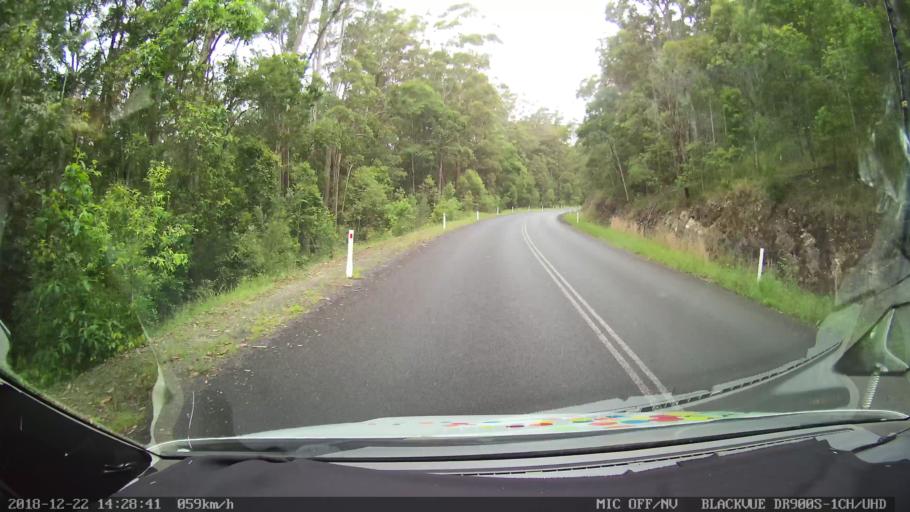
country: AU
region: New South Wales
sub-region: Bellingen
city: Dorrigo
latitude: -30.0747
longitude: 152.6370
